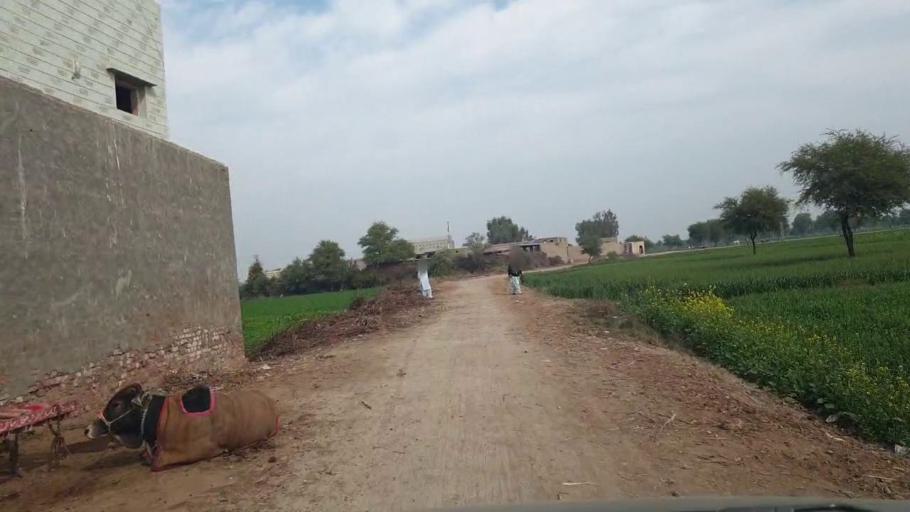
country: PK
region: Sindh
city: Shahdadpur
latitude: 25.9506
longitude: 68.7060
